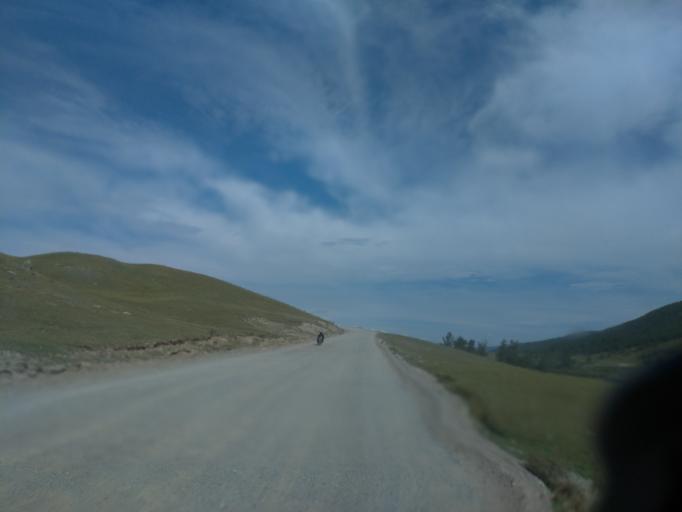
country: RU
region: Altay
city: Ust'-Ulagan
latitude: 50.7084
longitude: 88.0190
